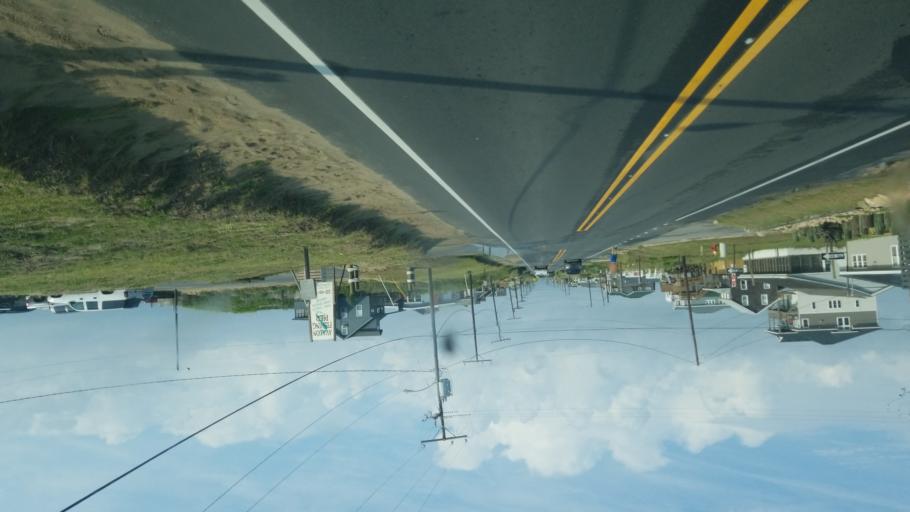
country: US
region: North Carolina
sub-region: Dare County
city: Kill Devil Hills
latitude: 36.0436
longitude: -75.6751
